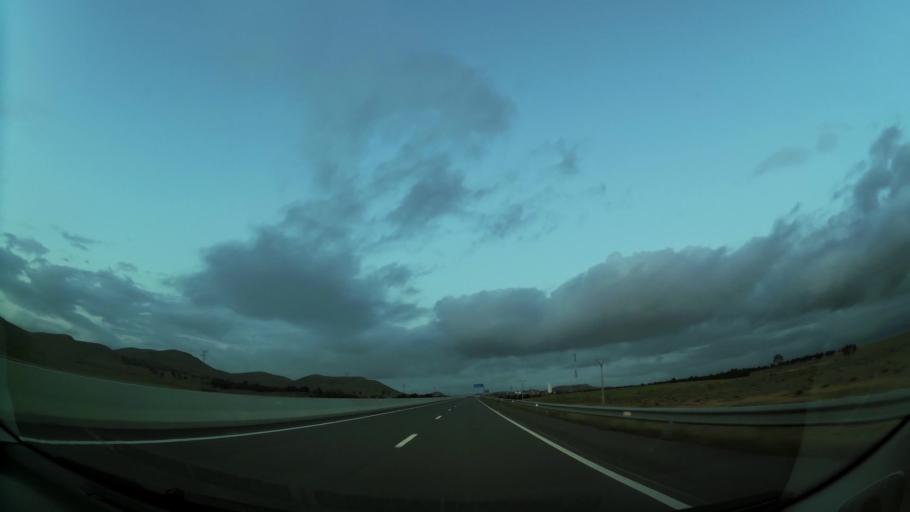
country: MA
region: Oriental
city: El Aioun
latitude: 34.6171
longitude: -2.4474
